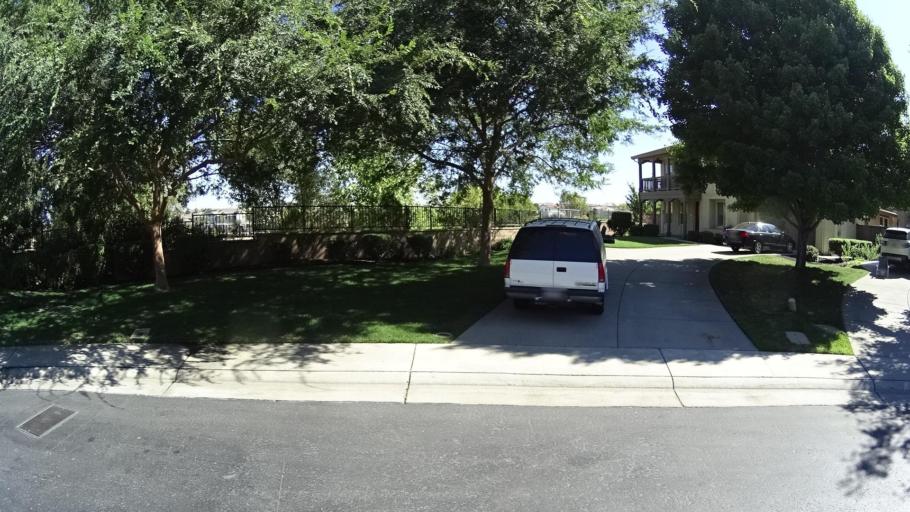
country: US
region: California
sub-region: Placer County
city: Rocklin
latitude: 38.8323
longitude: -121.2770
